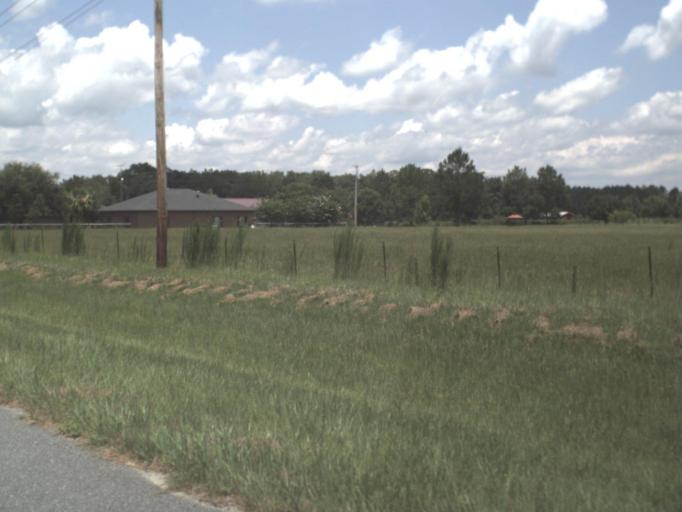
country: US
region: Florida
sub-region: Union County
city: Lake Butler
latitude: 30.0103
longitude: -82.4492
